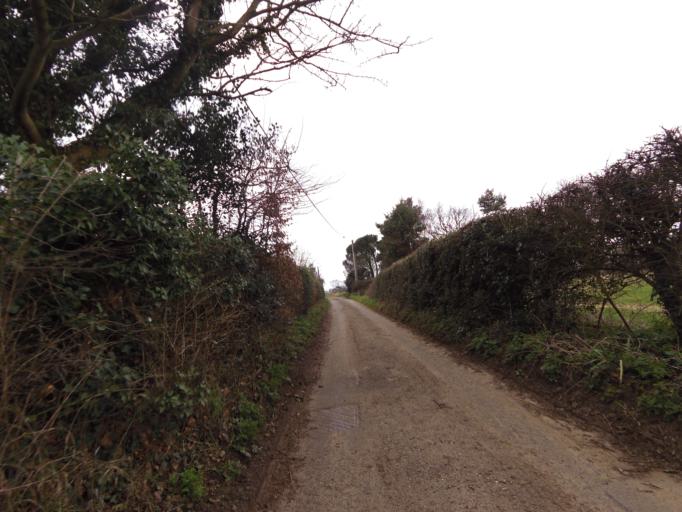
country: GB
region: England
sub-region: Suffolk
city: Woodbridge
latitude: 52.0575
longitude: 1.3255
